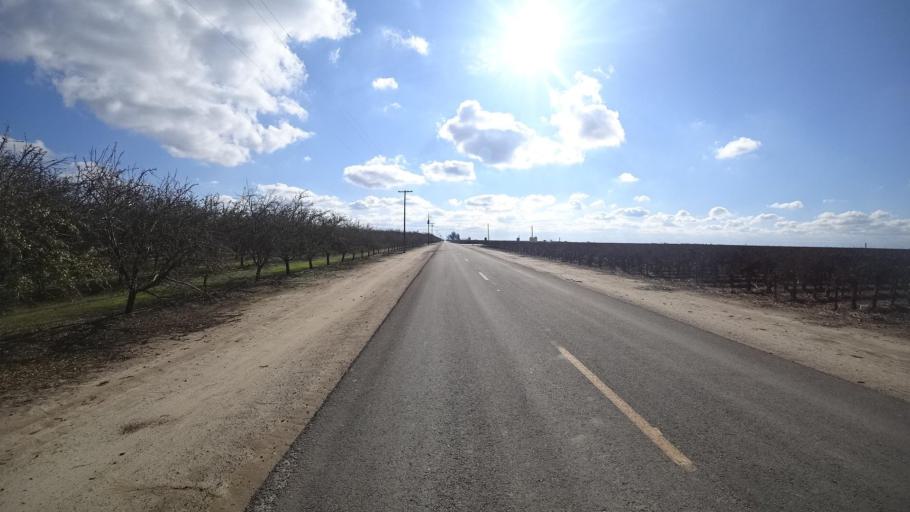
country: US
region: California
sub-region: Kern County
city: Delano
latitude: 35.7554
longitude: -119.3656
